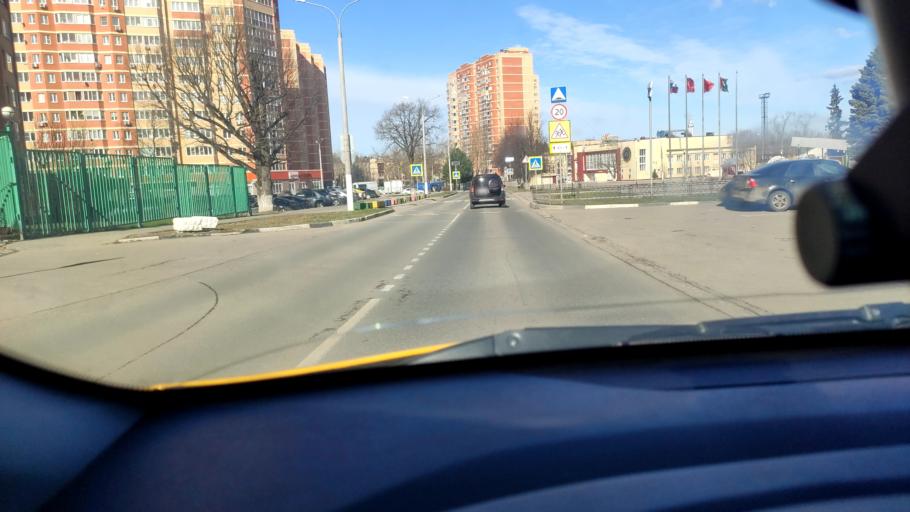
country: RU
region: Moskovskaya
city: Selyatino
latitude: 55.5143
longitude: 36.9871
